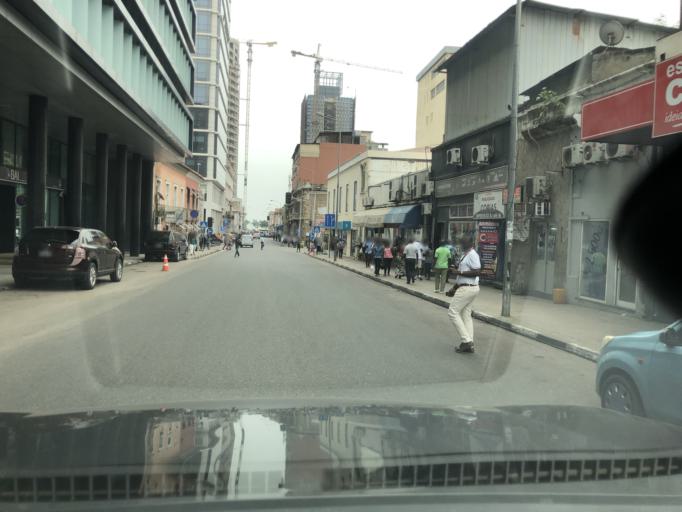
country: AO
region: Luanda
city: Luanda
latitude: -8.8144
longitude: 13.2324
